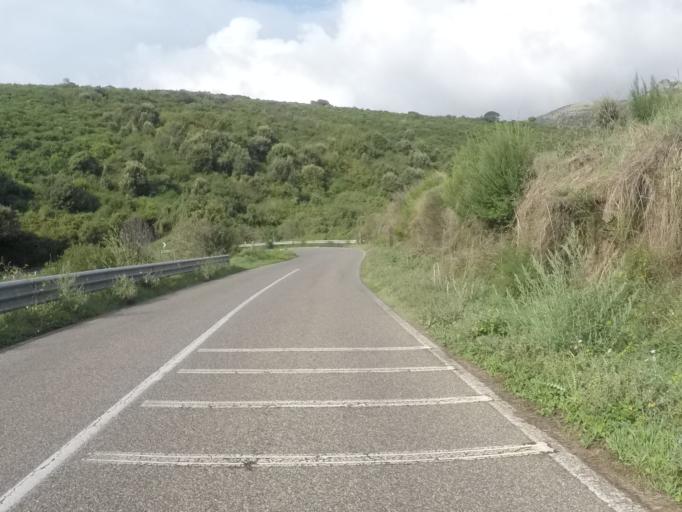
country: IT
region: Sardinia
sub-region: Provincia di Oristano
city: Santu Lussurgiu
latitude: 40.1476
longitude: 8.6559
